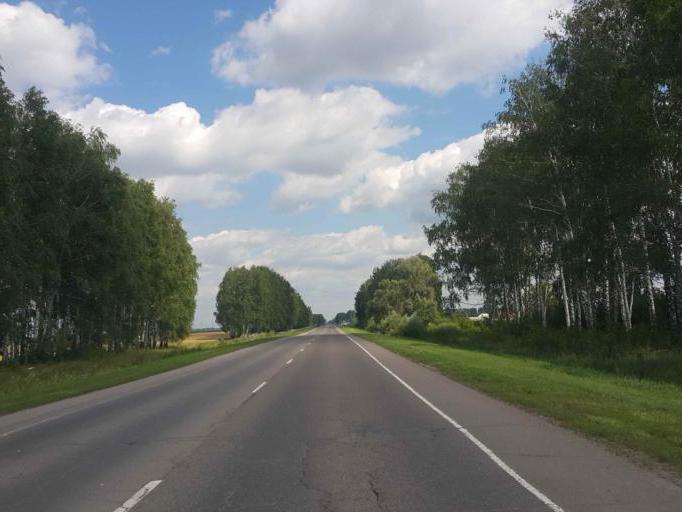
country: RU
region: Tambov
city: Goreloye
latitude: 53.0447
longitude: 41.4717
